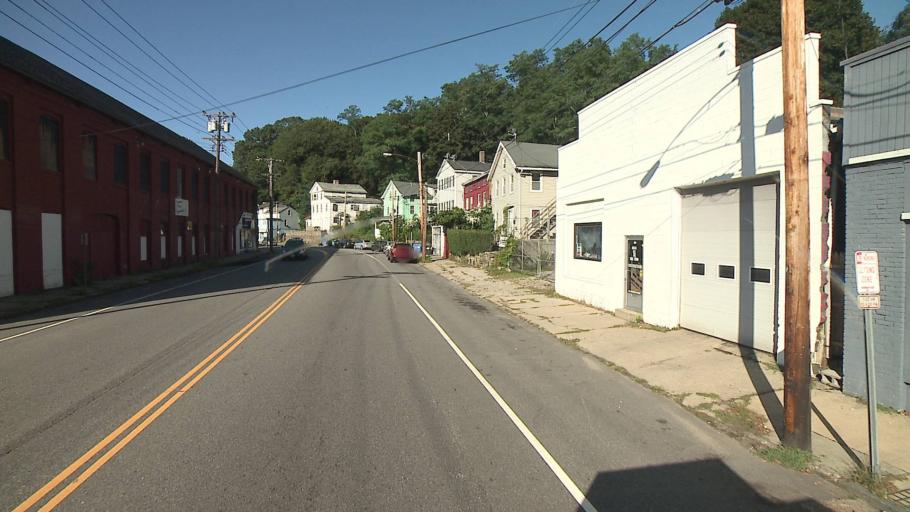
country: US
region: Connecticut
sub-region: New London County
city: Norwich
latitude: 41.5265
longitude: -72.0677
